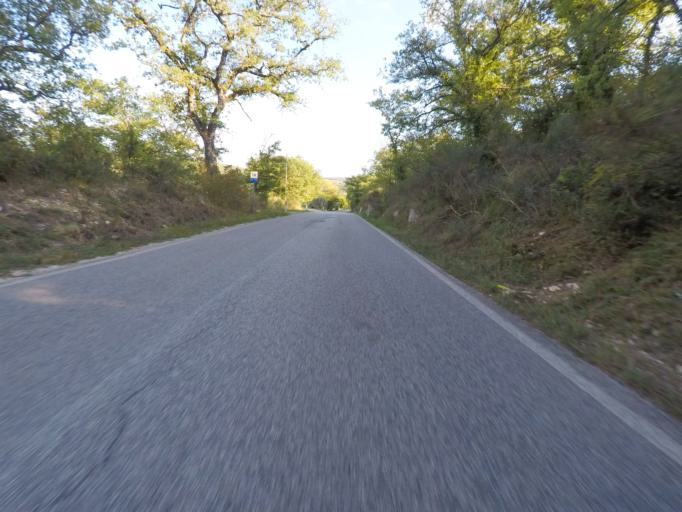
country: IT
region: Tuscany
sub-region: Provincia di Siena
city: Radda in Chianti
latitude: 43.4797
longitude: 11.3683
